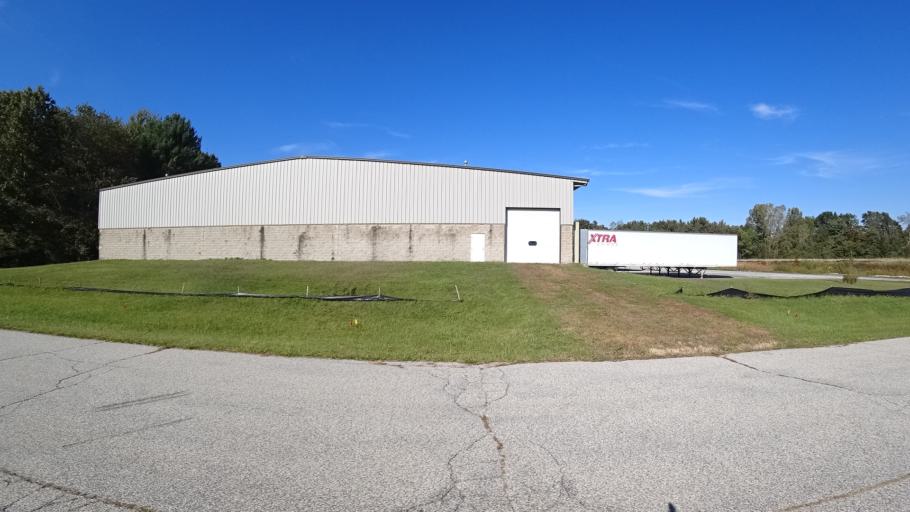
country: US
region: Indiana
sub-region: LaPorte County
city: Trail Creek
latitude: 41.6984
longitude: -86.8413
